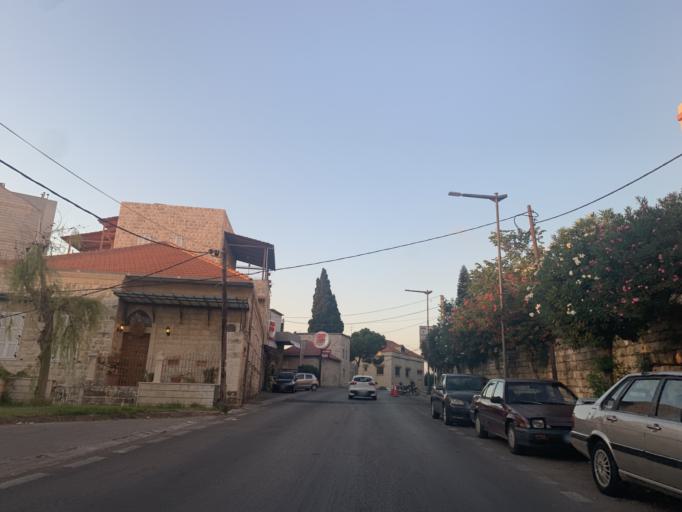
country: LB
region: Mont-Liban
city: Djounie
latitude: 33.9651
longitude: 35.6252
